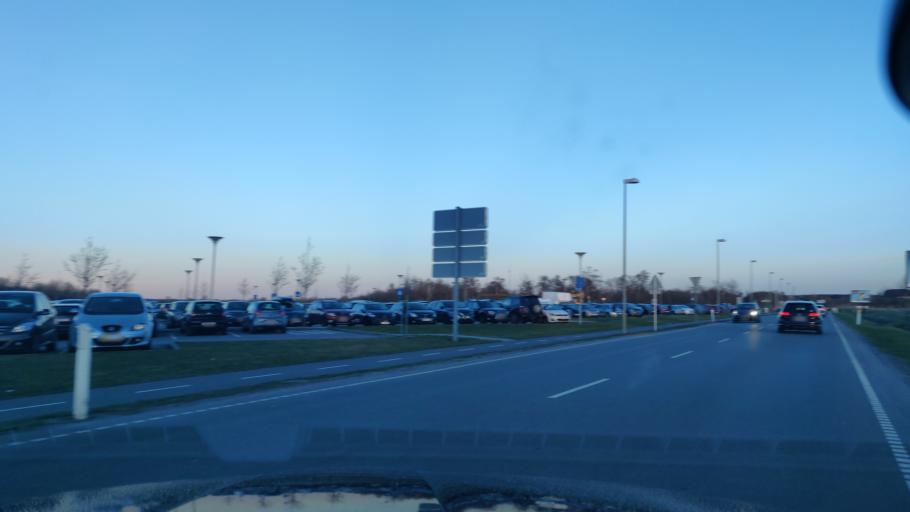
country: DK
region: North Denmark
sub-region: Alborg Kommune
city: Vadum
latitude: 57.0861
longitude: 9.8768
